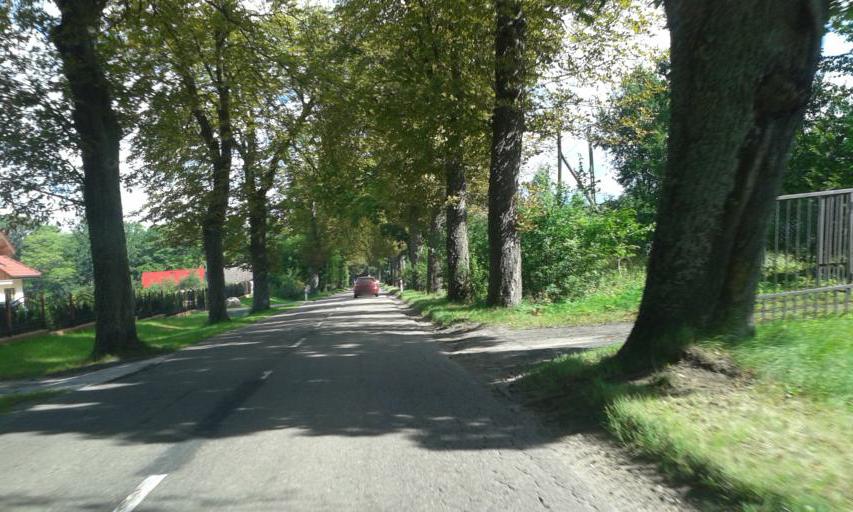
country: PL
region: West Pomeranian Voivodeship
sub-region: Powiat koszalinski
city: Polanow
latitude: 54.2081
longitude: 16.7005
